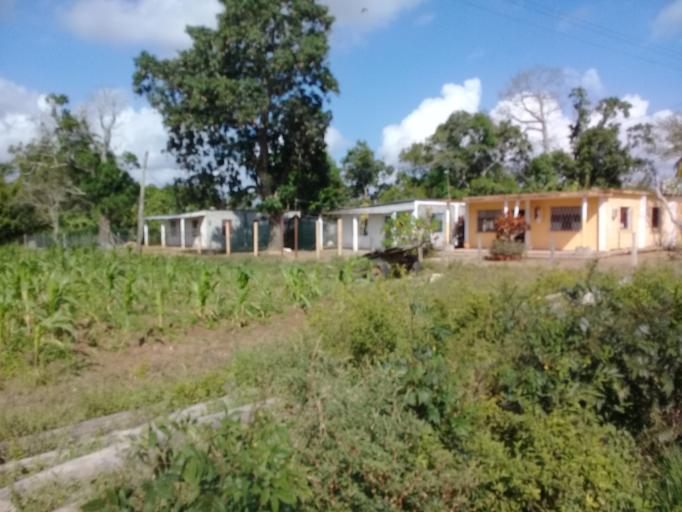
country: CU
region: Pinar del Rio
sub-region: Municipio de Pinar del Rio
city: Pinar del Rio
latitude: 22.3497
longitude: -83.6625
